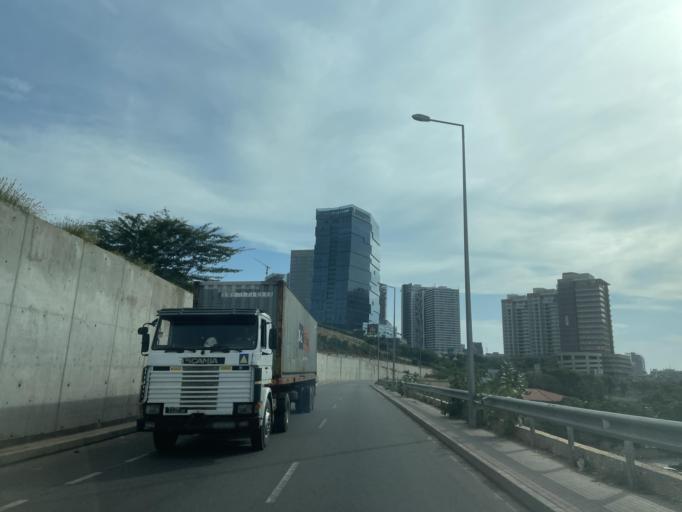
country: AO
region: Luanda
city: Luanda
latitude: -8.8088
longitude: 13.2447
